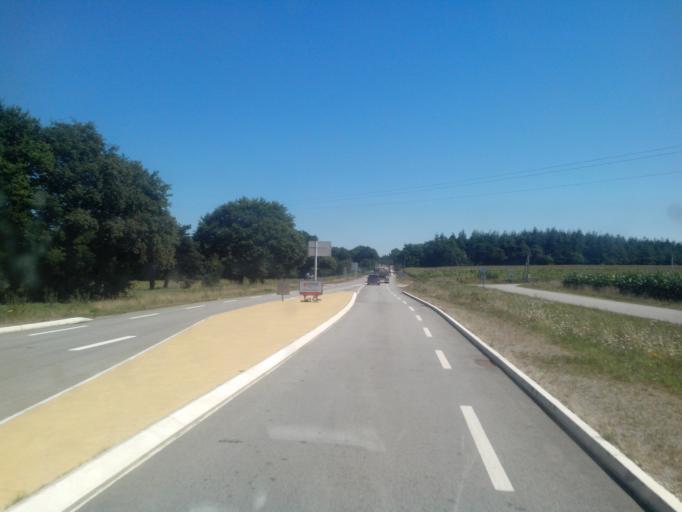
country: FR
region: Brittany
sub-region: Departement du Morbihan
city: Guillac
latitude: 47.8729
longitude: -2.4941
